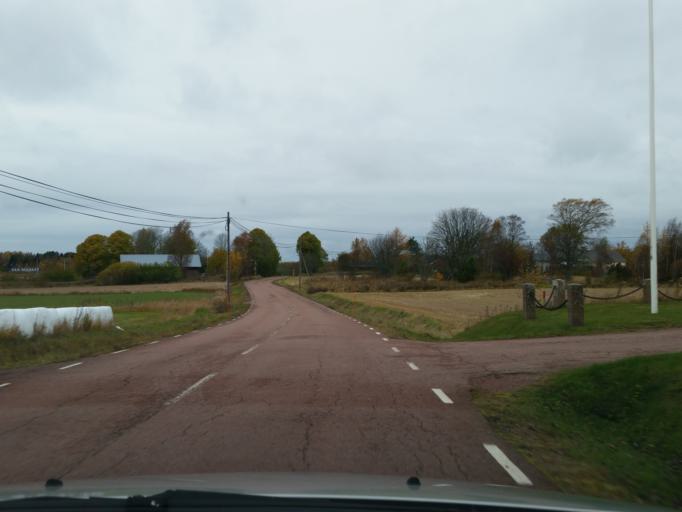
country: AX
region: Alands landsbygd
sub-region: Lemland
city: Lemland
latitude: 60.0718
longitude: 20.0906
